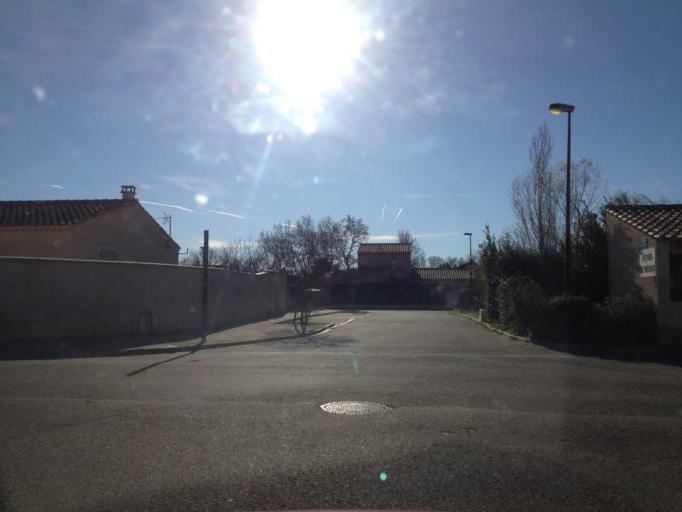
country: FR
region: Provence-Alpes-Cote d'Azur
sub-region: Departement du Vaucluse
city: Orange
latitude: 44.1454
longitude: 4.7963
